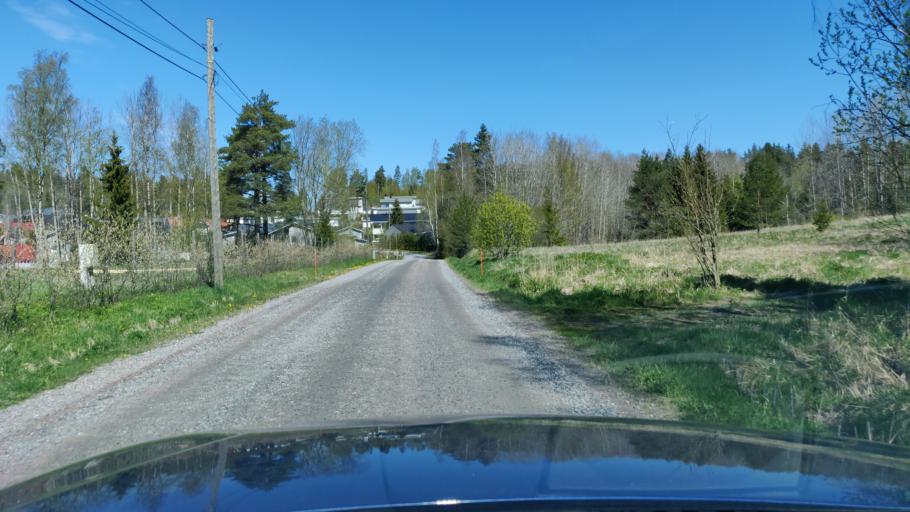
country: FI
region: Uusimaa
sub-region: Helsinki
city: Nurmijaervi
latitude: 60.3601
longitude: 24.7562
